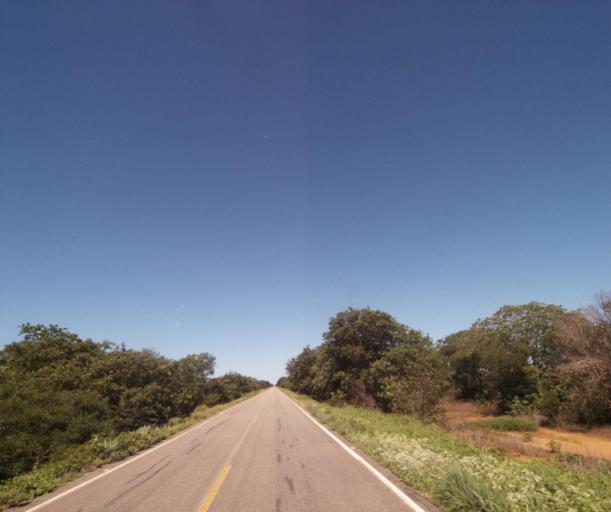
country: BR
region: Bahia
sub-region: Palmas De Monte Alto
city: Palmas de Monte Alto
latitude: -14.2621
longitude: -43.3171
